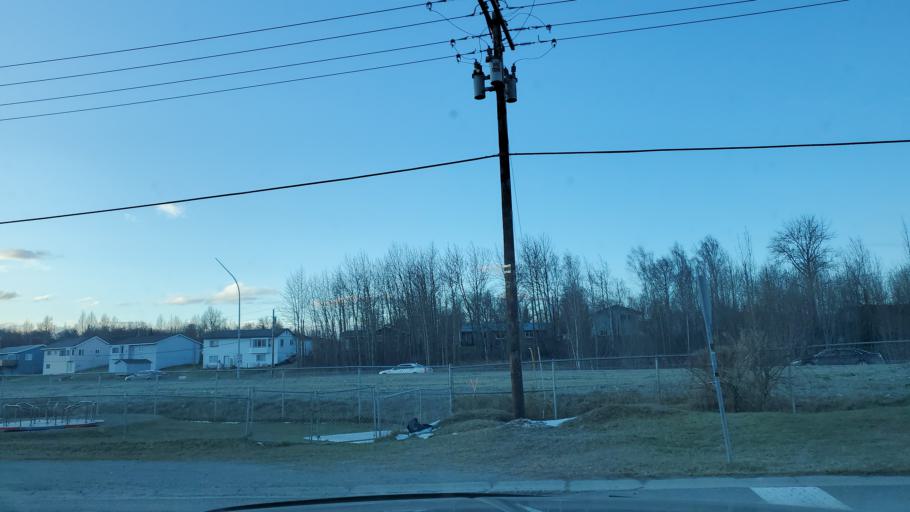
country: US
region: Alaska
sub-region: Matanuska-Susitna Borough
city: Palmer
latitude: 61.6058
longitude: -149.1181
